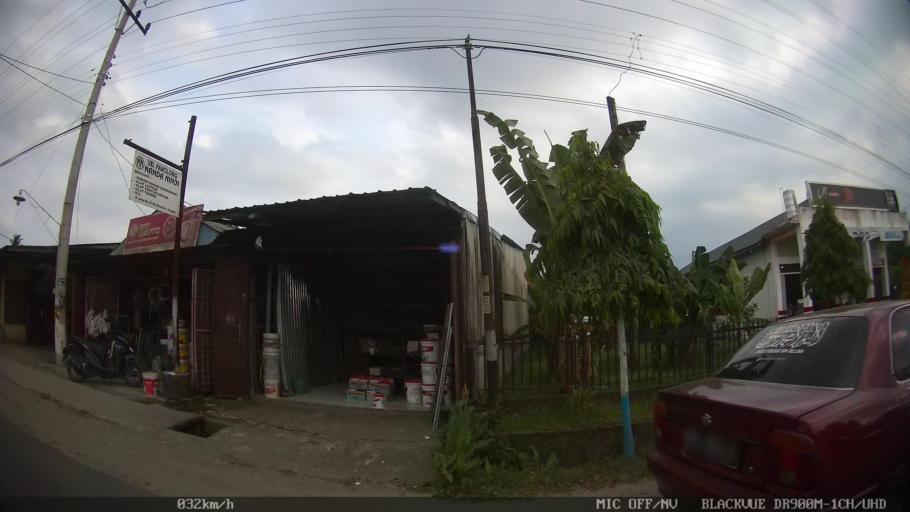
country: ID
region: North Sumatra
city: Sunggal
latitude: 3.5604
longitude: 98.5623
